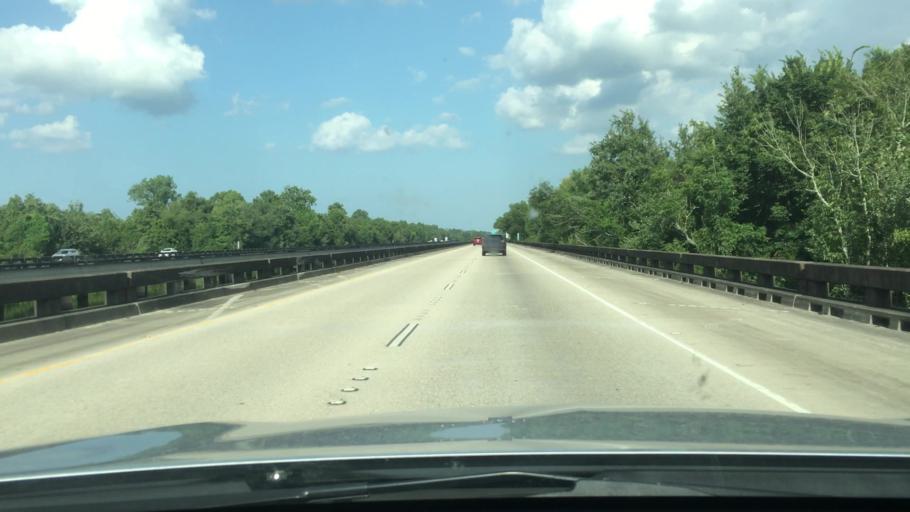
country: US
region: Louisiana
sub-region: Saint John the Baptist Parish
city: Montegut
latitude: 30.1087
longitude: -90.5212
